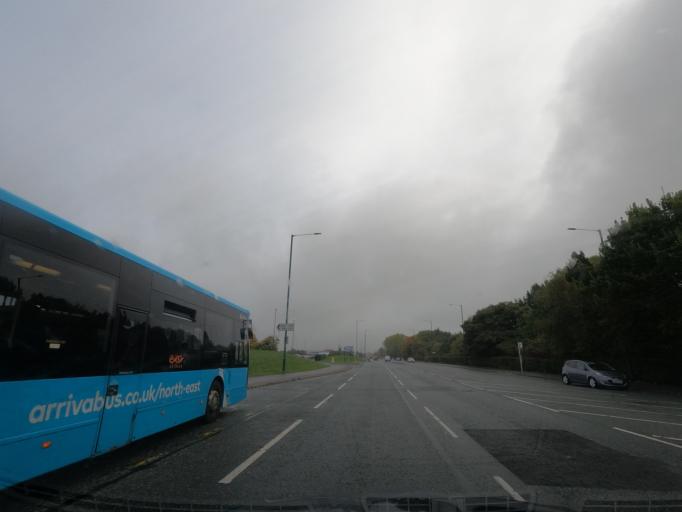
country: GB
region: England
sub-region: Redcar and Cleveland
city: South Bank
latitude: 54.5706
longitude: -1.1657
